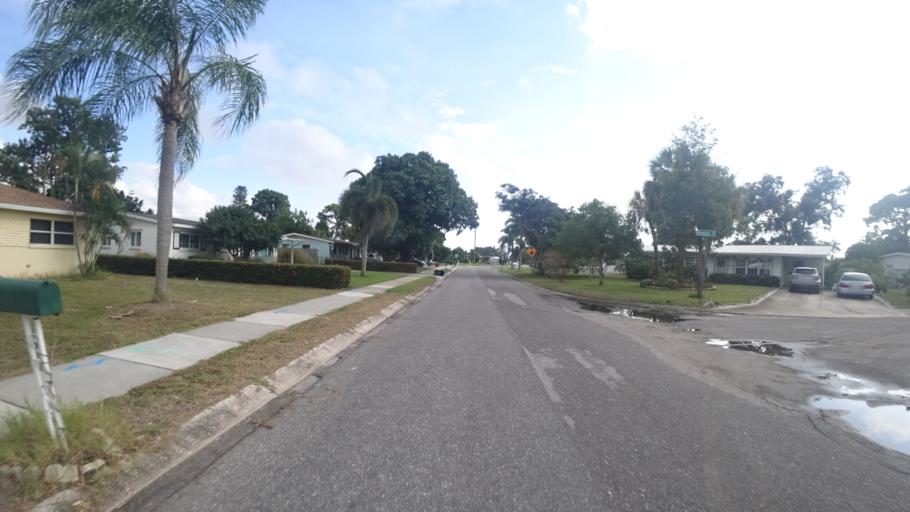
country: US
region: Florida
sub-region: Manatee County
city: Bayshore Gardens
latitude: 27.4240
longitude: -82.5903
